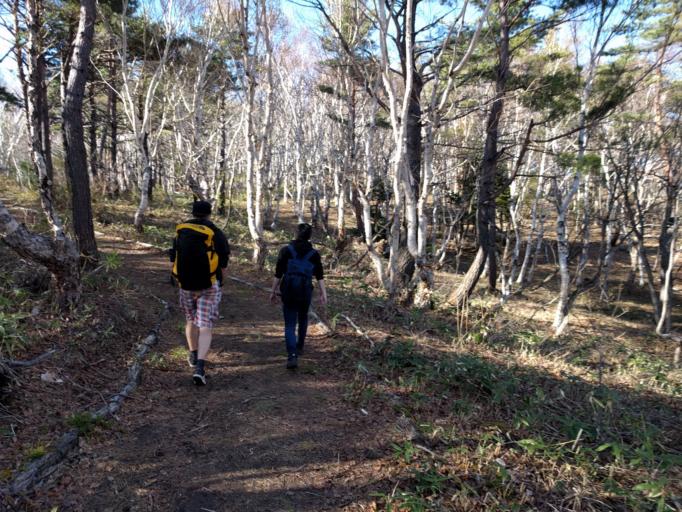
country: JP
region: Nagano
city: Nakano
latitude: 36.7219
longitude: 138.4776
